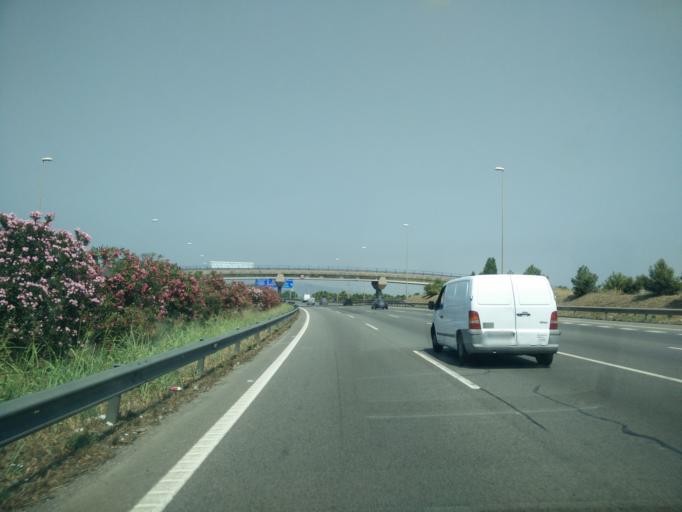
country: ES
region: Catalonia
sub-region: Provincia de Barcelona
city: Sant Feliu de Llobregat
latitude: 41.3662
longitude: 2.0486
